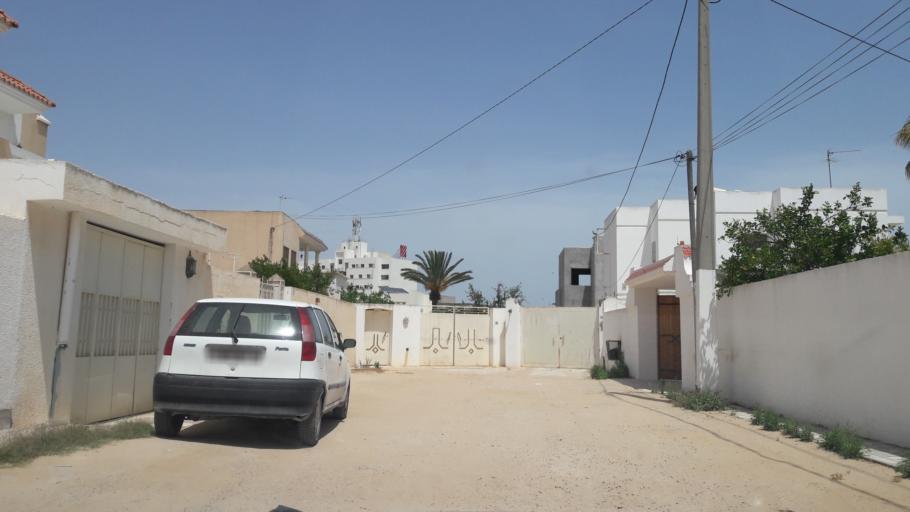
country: TN
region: Safaqis
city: Sfax
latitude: 34.7762
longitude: 10.7585
